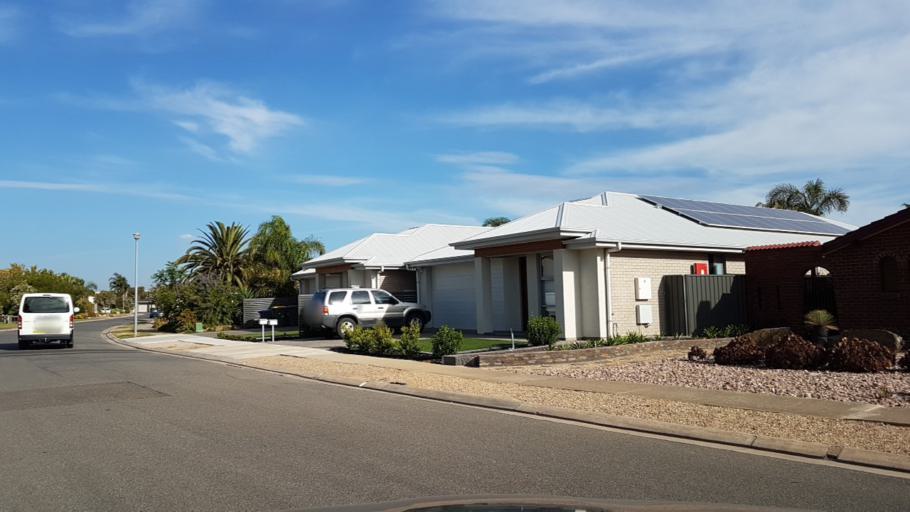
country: AU
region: South Australia
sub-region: Charles Sturt
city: West Lakes Shore
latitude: -34.8606
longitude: 138.4852
